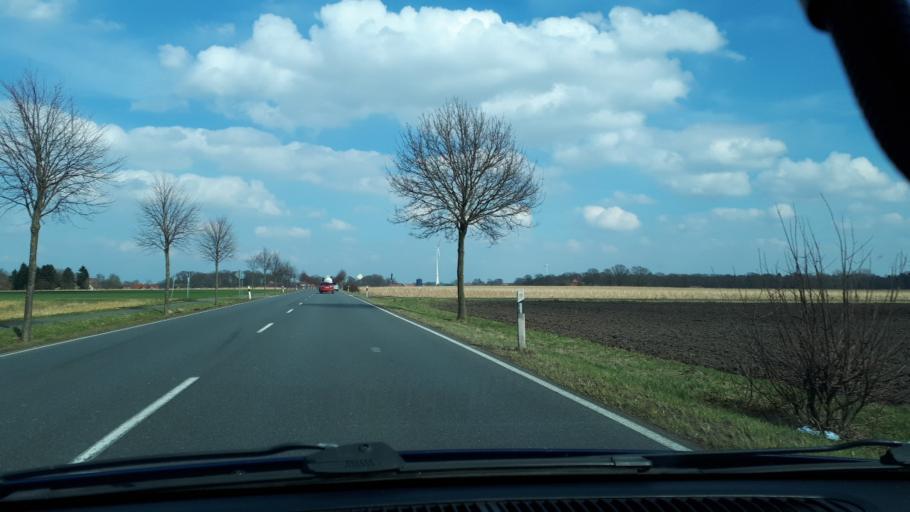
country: DE
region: Lower Saxony
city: Varrel
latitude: 52.6493
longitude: 8.7417
